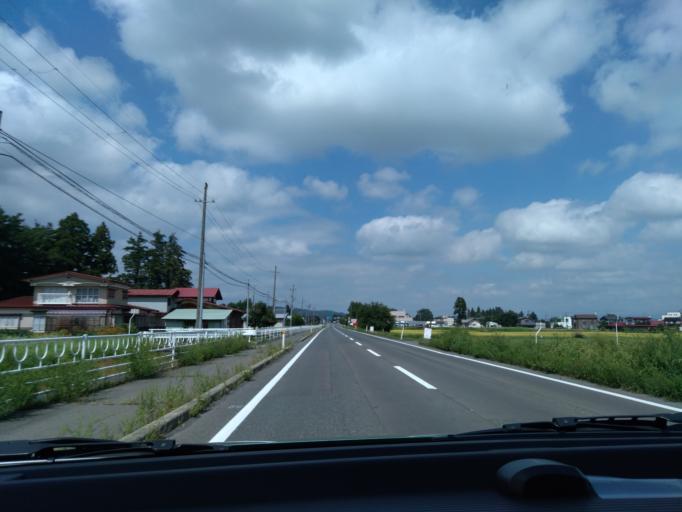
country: JP
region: Iwate
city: Morioka-shi
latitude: 39.5496
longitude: 141.1040
